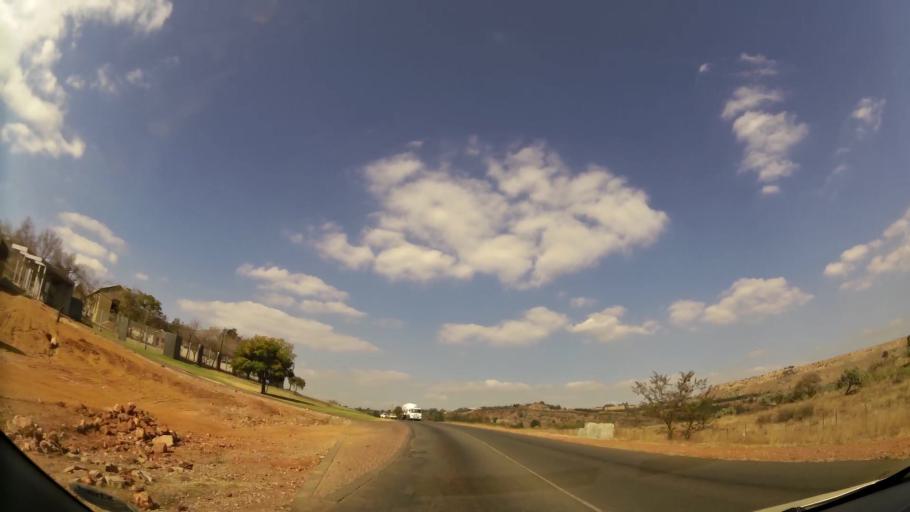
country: ZA
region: Gauteng
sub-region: West Rand District Municipality
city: Krugersdorp
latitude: -26.0435
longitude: 27.7454
